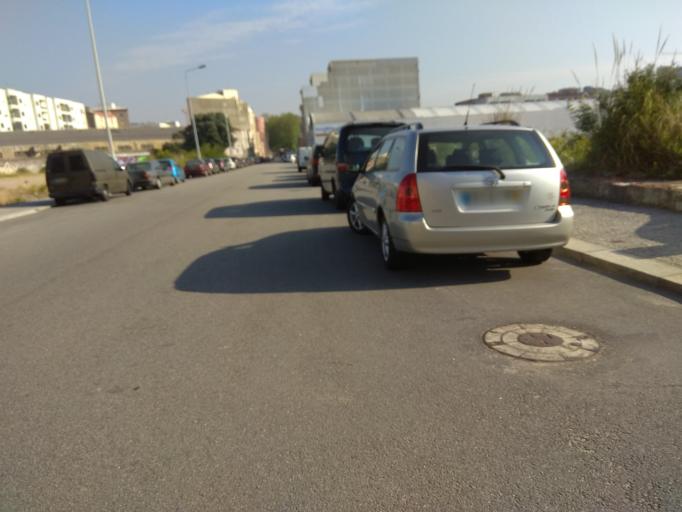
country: PT
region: Porto
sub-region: Matosinhos
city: Matosinhos
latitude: 41.1748
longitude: -8.6849
